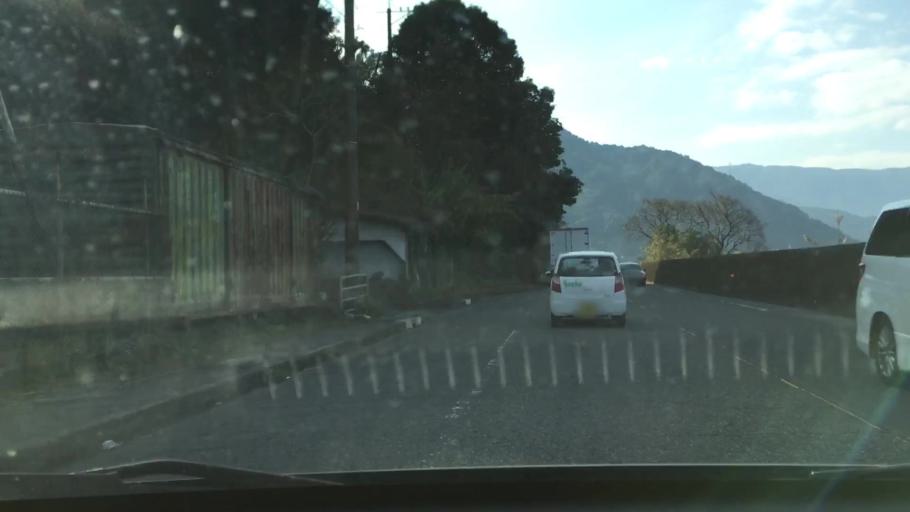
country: JP
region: Kagoshima
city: Tarumizu
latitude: 31.5891
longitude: 130.7879
